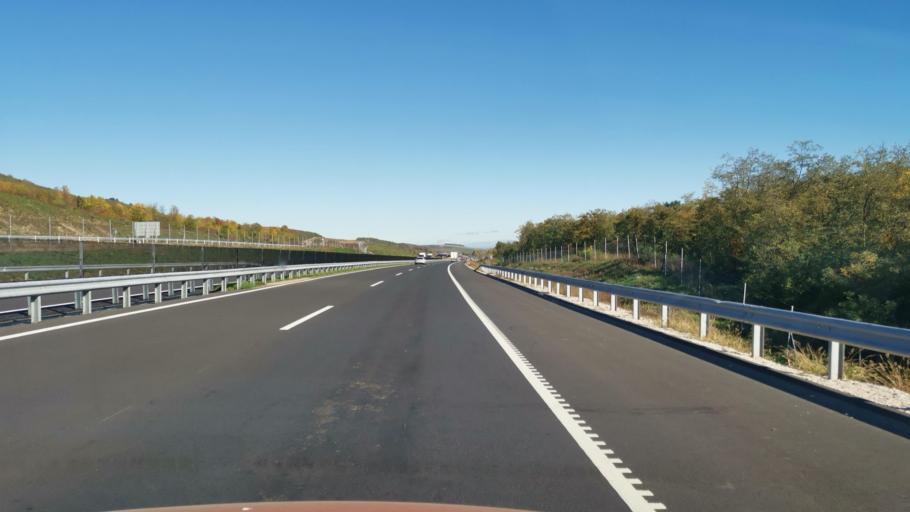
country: HU
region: Borsod-Abauj-Zemplen
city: Gonc
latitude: 48.4721
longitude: 21.2029
